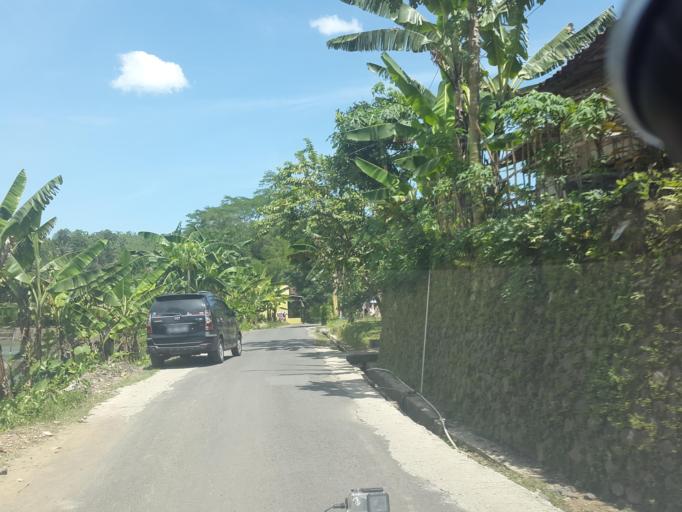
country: ID
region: Central Java
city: Sangkalputung
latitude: -7.4140
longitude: 109.0519
